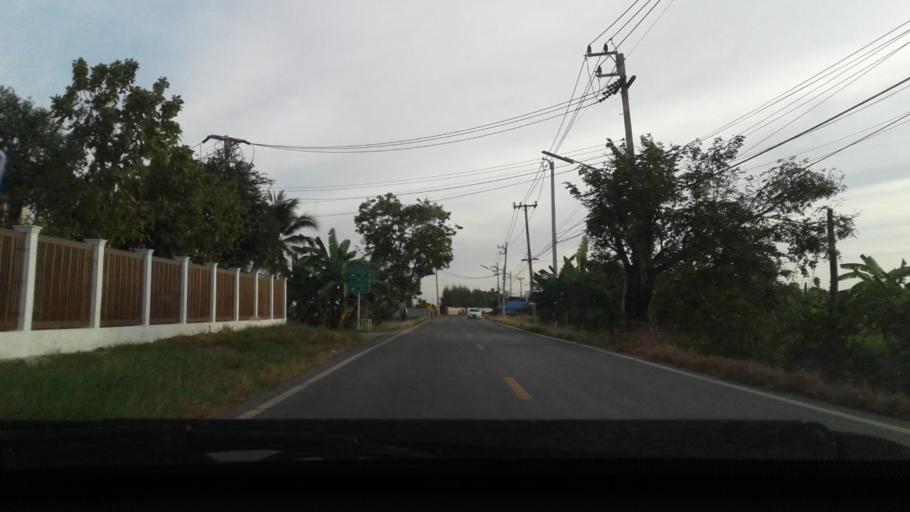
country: TH
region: Nonthaburi
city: Sai Noi
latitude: 13.9152
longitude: 100.2558
